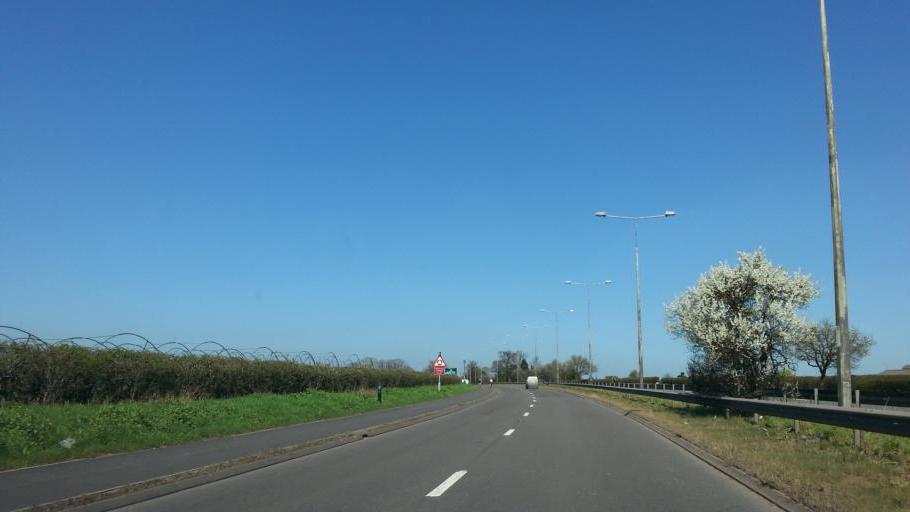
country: GB
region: England
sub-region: Staffordshire
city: Penkridge
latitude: 52.6892
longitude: -2.1323
